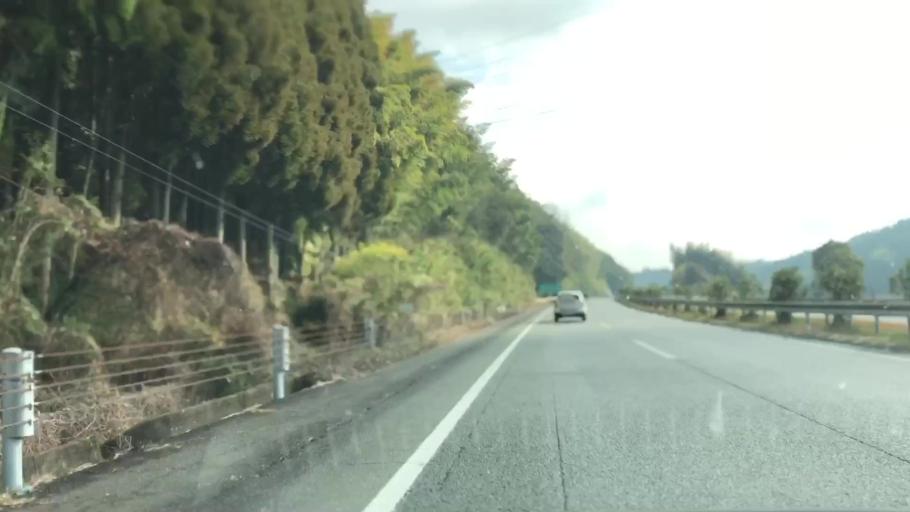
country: JP
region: Kumamoto
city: Yamaga
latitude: 33.0388
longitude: 130.5704
